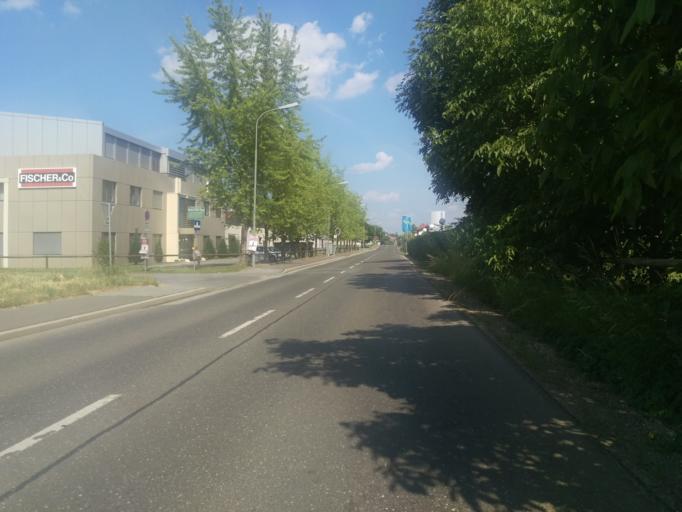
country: AT
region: Styria
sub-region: Politischer Bezirk Graz-Umgebung
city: Seiersberg
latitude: 47.0249
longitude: 15.4038
